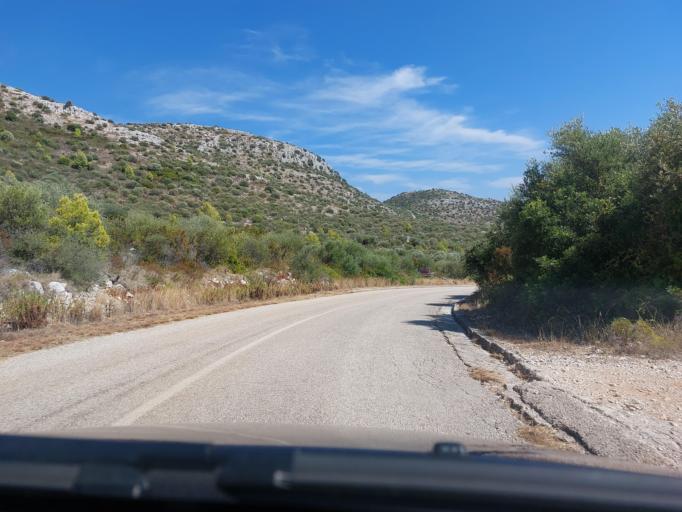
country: HR
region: Dubrovacko-Neretvanska
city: Smokvica
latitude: 42.7436
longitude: 16.8830
